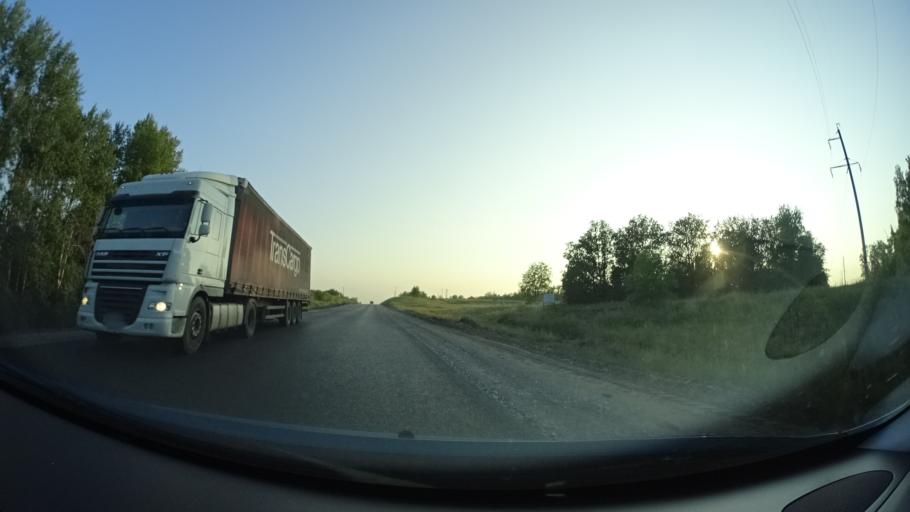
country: RU
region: Samara
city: Isakly
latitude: 53.9855
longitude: 51.5023
